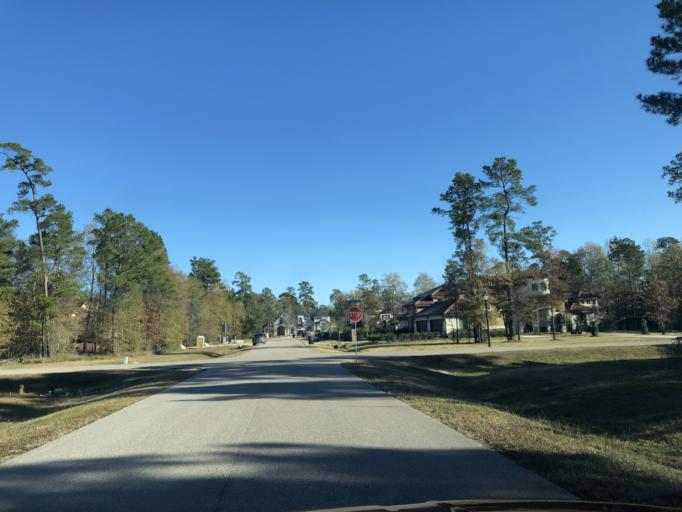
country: US
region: Texas
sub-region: Montgomery County
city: Porter Heights
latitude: 30.0748
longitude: -95.3336
